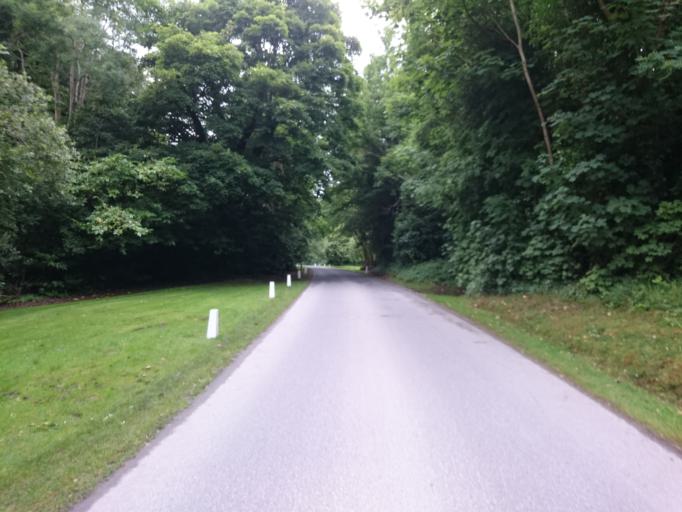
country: IE
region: Connaught
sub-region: Maigh Eo
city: Ballinrobe
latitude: 53.5359
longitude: -9.2835
